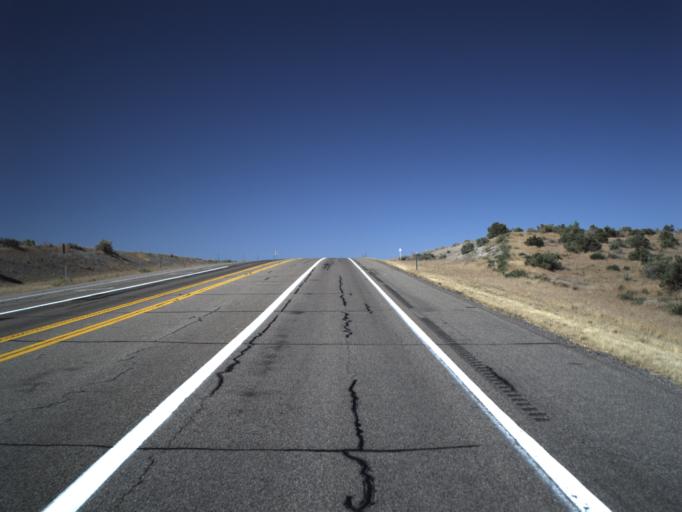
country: US
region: Utah
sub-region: Millard County
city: Delta
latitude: 39.3957
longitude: -112.5049
